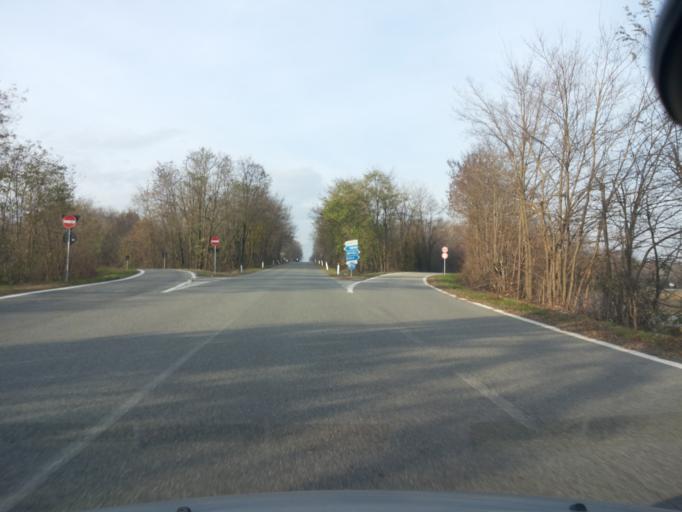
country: IT
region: Piedmont
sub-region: Provincia di Biella
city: Verrone
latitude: 45.4860
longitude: 8.1142
